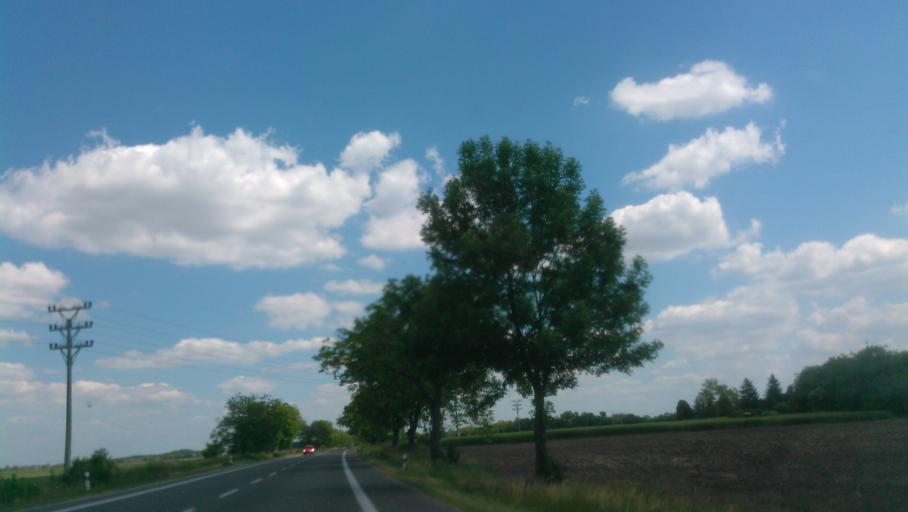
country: SK
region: Trnavsky
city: Samorin
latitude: 48.0026
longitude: 17.4027
